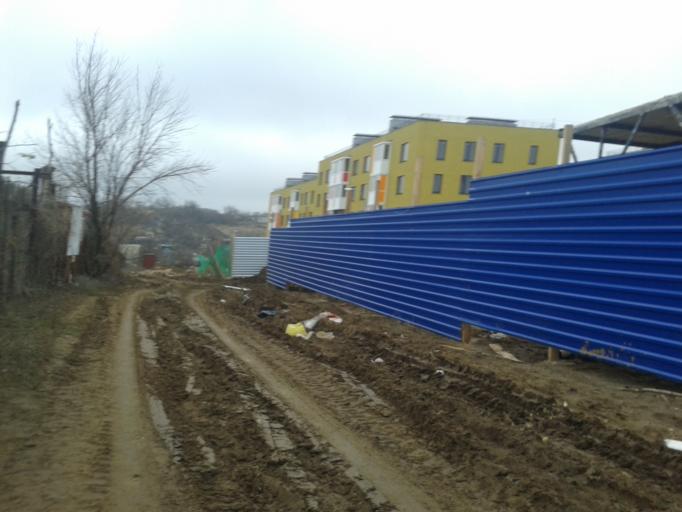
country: RU
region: Volgograd
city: Volgograd
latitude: 48.6644
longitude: 44.4075
